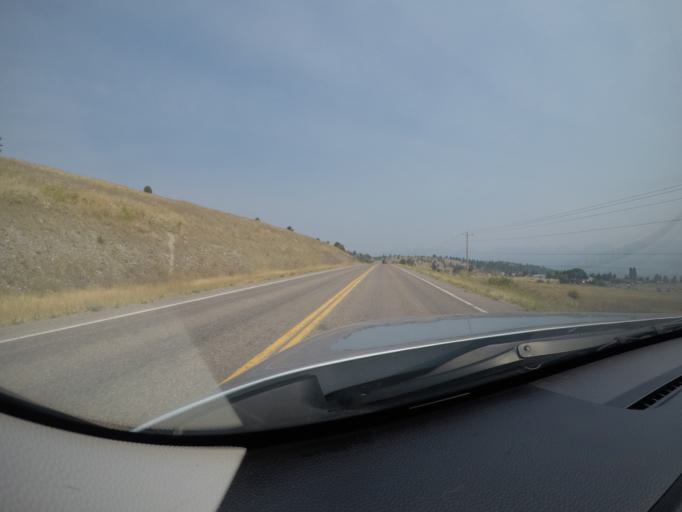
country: US
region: Montana
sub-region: Lake County
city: Polson
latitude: 47.7371
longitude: -114.1843
